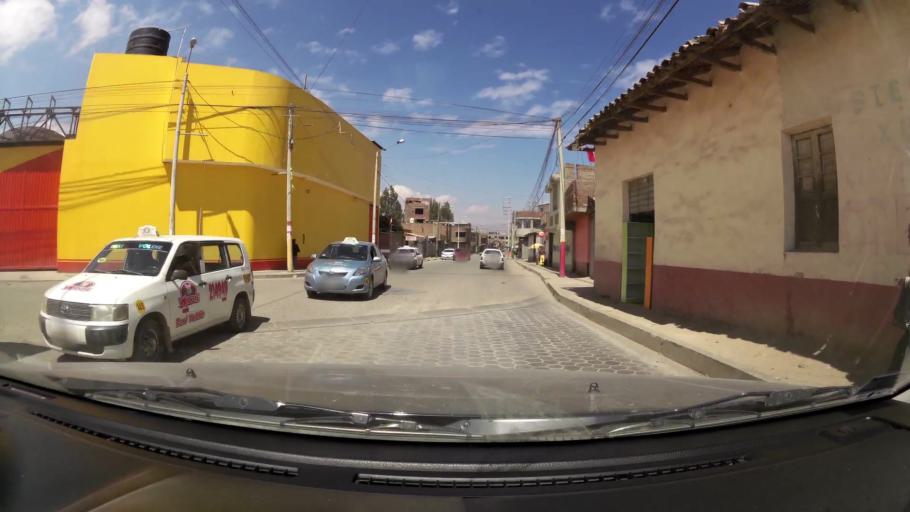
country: PE
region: Junin
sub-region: Provincia de Huancayo
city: El Tambo
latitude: -12.0841
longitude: -75.2123
